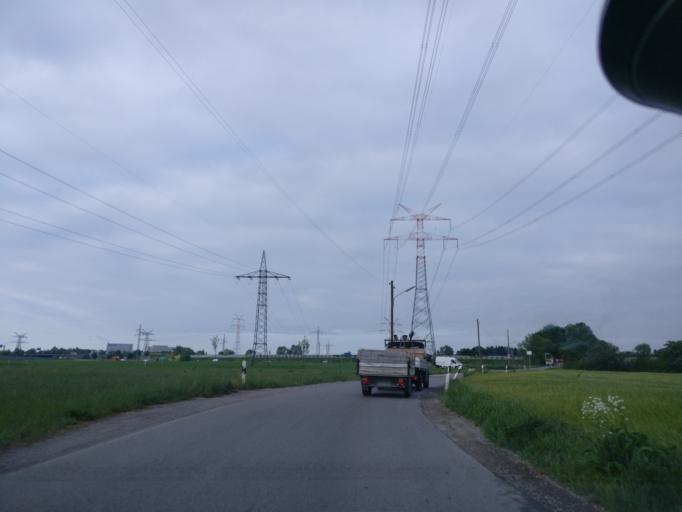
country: DE
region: Bavaria
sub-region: Upper Bavaria
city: Karlsfeld
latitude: 48.1875
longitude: 11.4307
